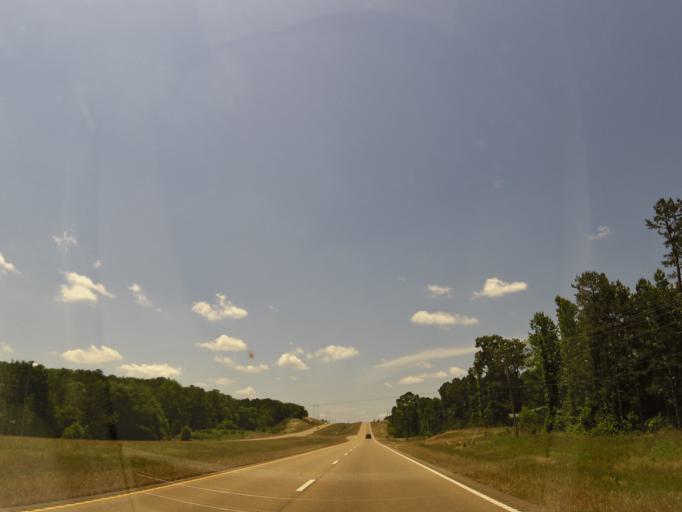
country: US
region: Mississippi
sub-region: Lafayette County
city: Oxford
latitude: 34.3154
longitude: -89.3405
